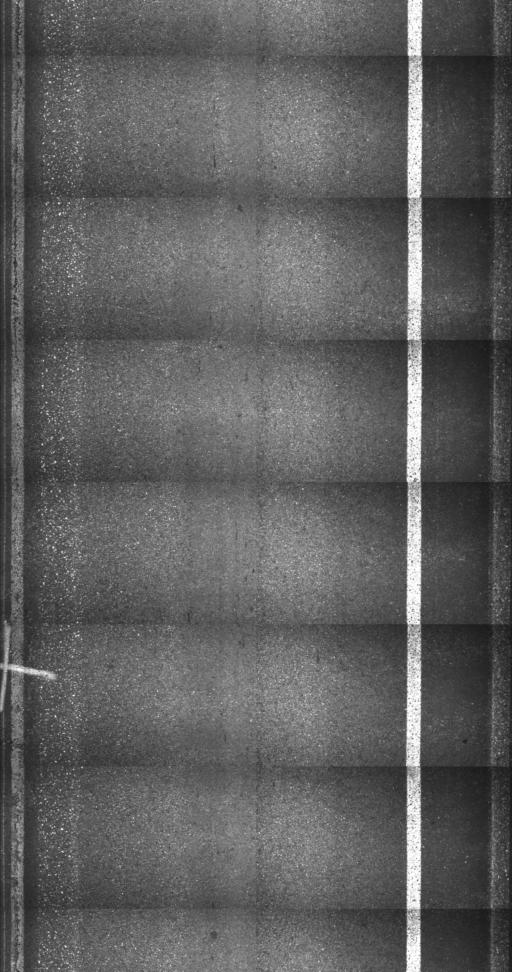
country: CA
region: Quebec
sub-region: Monteregie
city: Sutton
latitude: 44.9876
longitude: -72.4964
